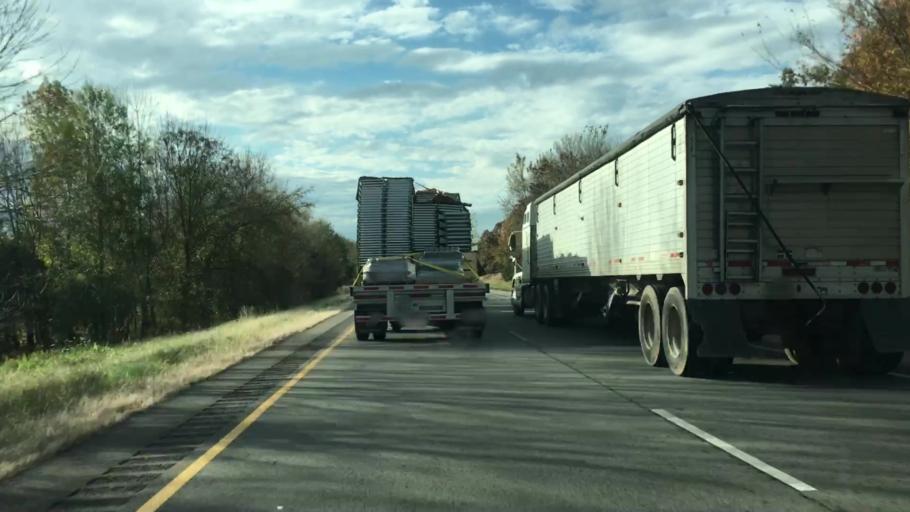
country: US
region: Arkansas
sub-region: Pope County
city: Pottsville
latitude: 35.2465
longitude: -93.0018
